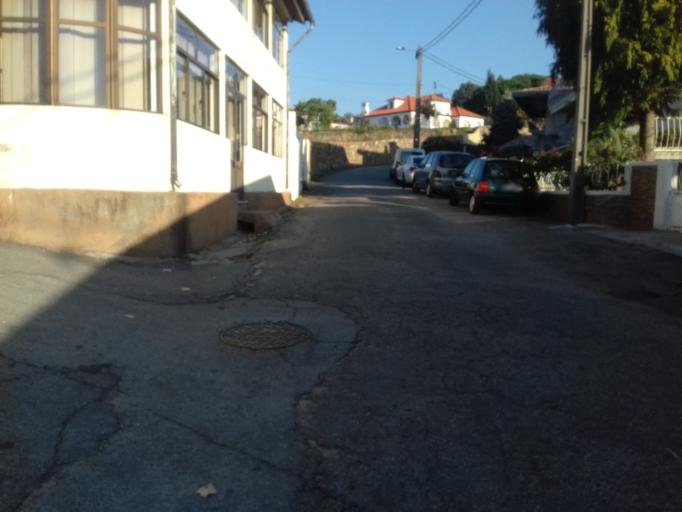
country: PT
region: Aveiro
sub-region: Albergaria-A-Velha
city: Branca
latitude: 40.7823
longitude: -8.4697
